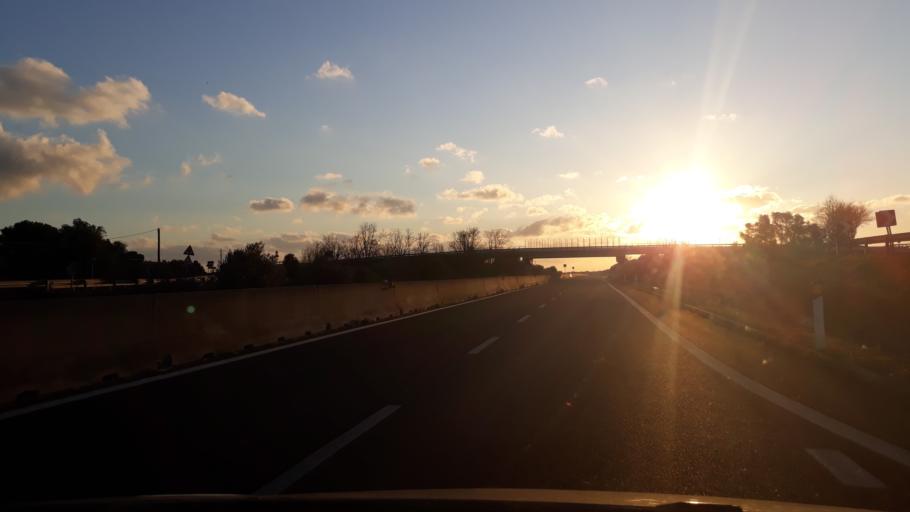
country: IT
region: Apulia
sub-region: Provincia di Brindisi
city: Ostuni
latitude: 40.7722
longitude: 17.6170
